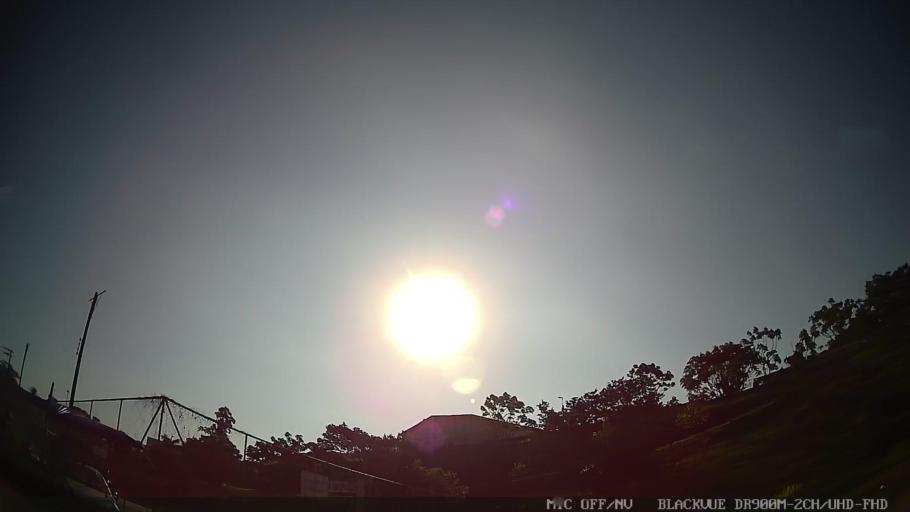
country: BR
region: Sao Paulo
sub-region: Ferraz De Vasconcelos
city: Ferraz de Vasconcelos
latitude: -23.5379
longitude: -46.4309
